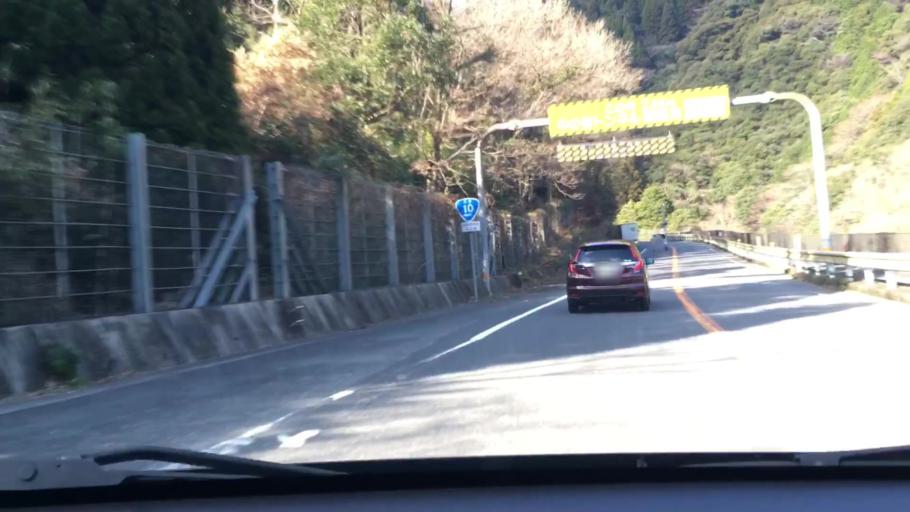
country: JP
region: Oita
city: Tsukumiura
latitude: 33.0011
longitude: 131.8038
